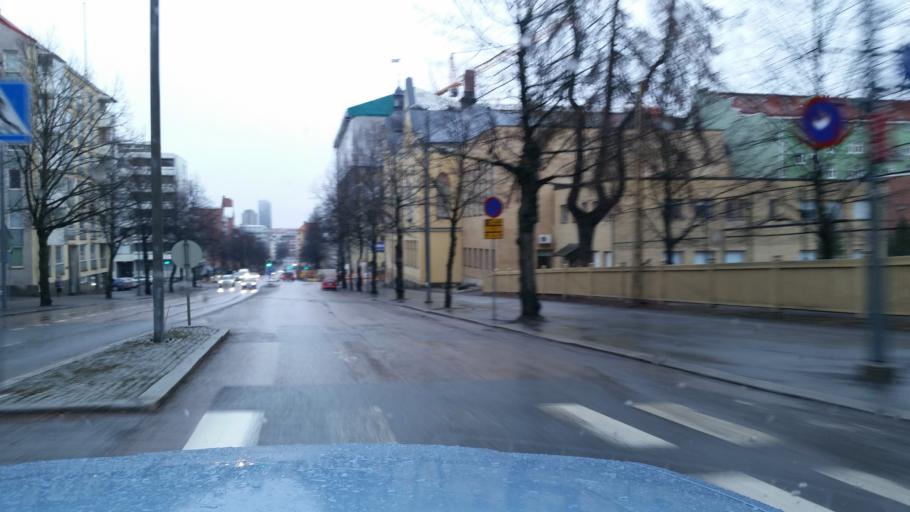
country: FI
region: Pirkanmaa
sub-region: Tampere
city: Tampere
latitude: 61.4941
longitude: 23.7455
